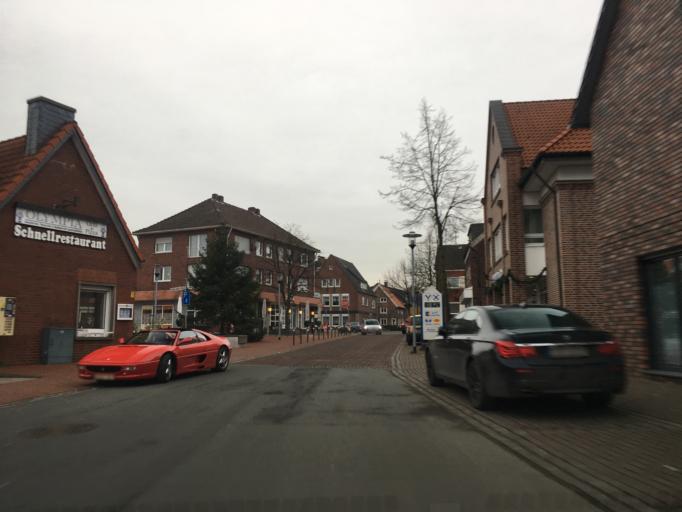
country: DE
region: North Rhine-Westphalia
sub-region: Regierungsbezirk Munster
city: Nordkirchen
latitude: 51.7385
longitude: 7.5244
